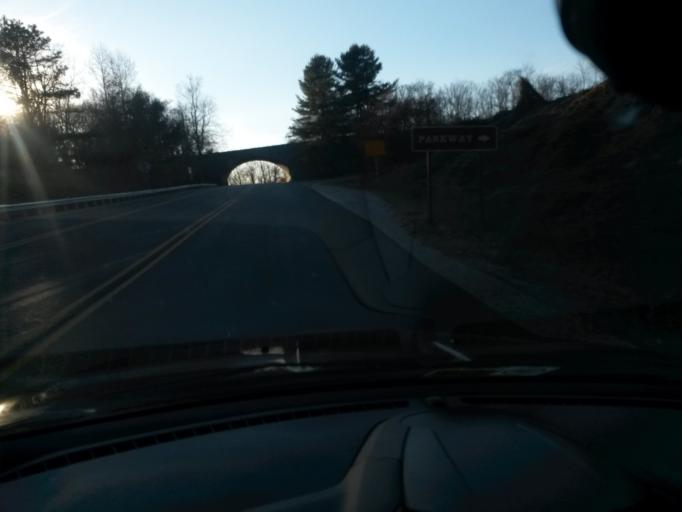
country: US
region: Virginia
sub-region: City of Buena Vista
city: Buena Vista
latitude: 37.7412
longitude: -79.3013
